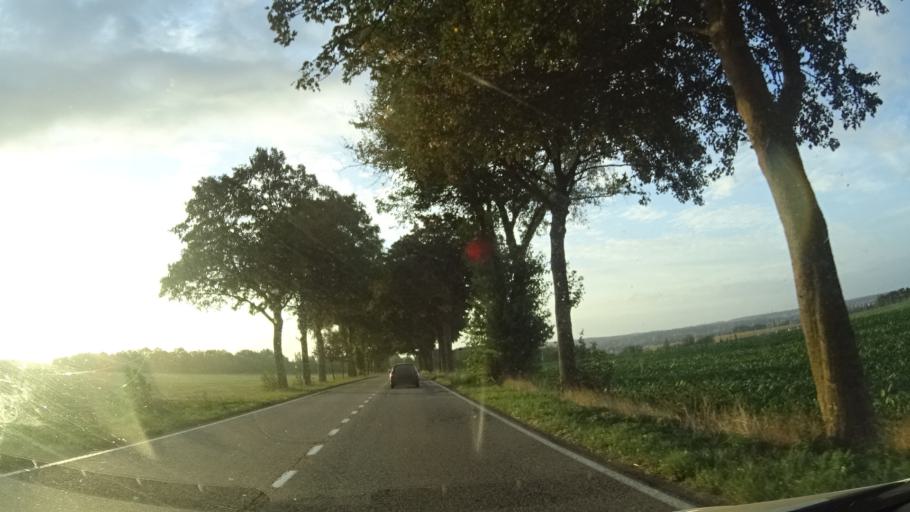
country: BE
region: Wallonia
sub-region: Province du Hainaut
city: Erquelinnes
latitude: 50.3255
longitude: 4.1120
